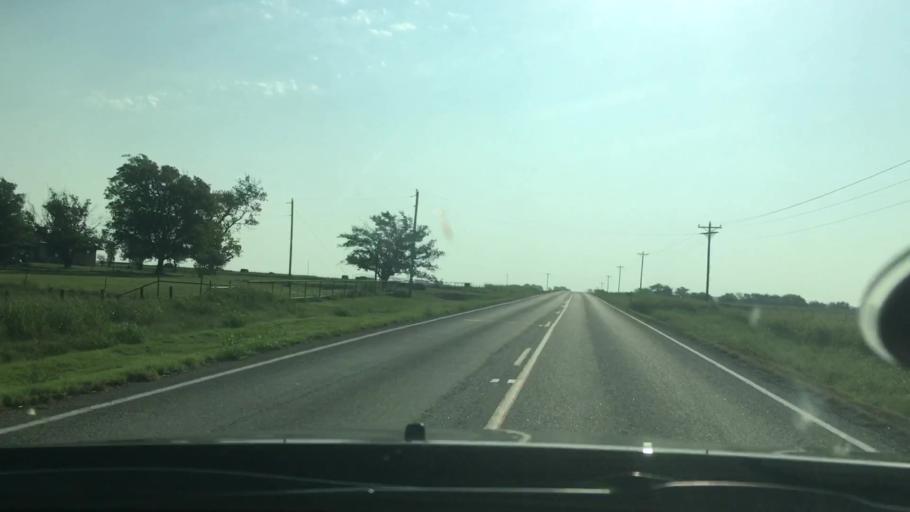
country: US
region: Oklahoma
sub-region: Bryan County
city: Durant
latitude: 34.1427
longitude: -96.3431
